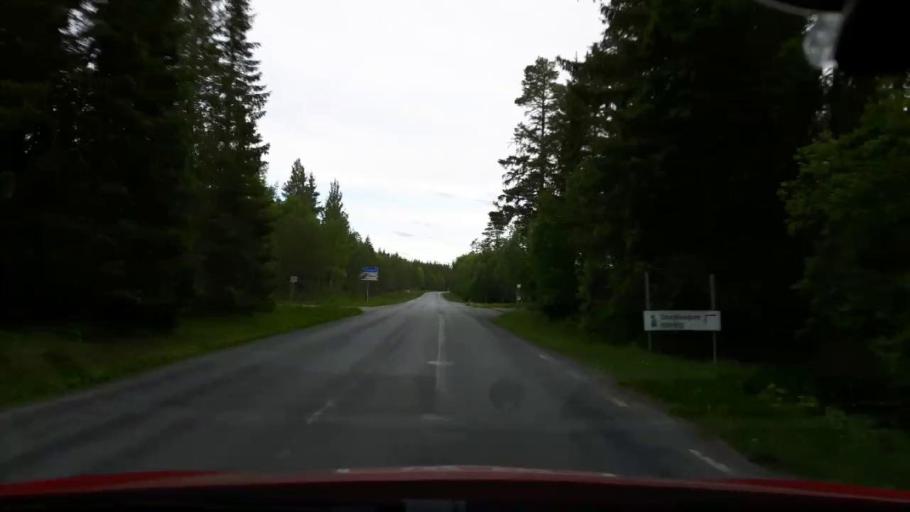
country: SE
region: Jaemtland
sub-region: OEstersunds Kommun
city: Ostersund
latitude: 63.1257
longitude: 14.4440
